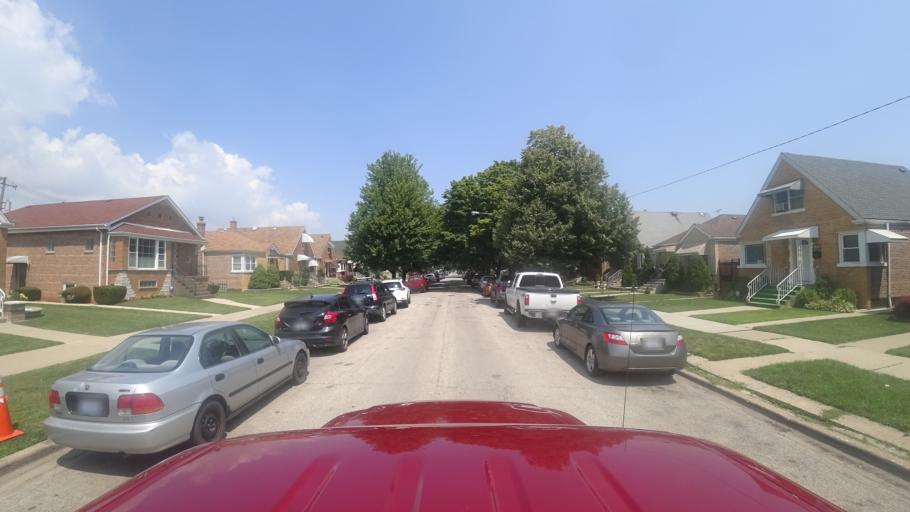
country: US
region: Illinois
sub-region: Cook County
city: Hometown
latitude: 41.7941
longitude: -87.7219
